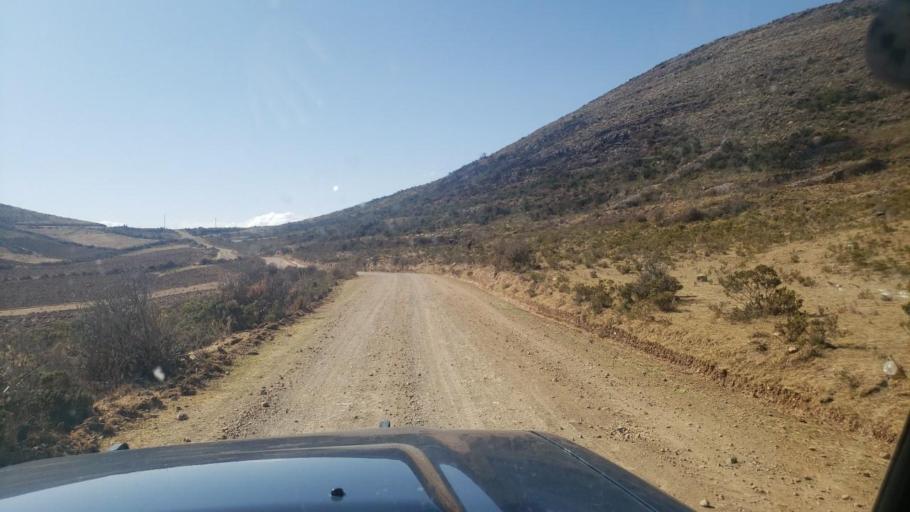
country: BO
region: La Paz
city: Huatajata
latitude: -16.3317
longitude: -68.6923
